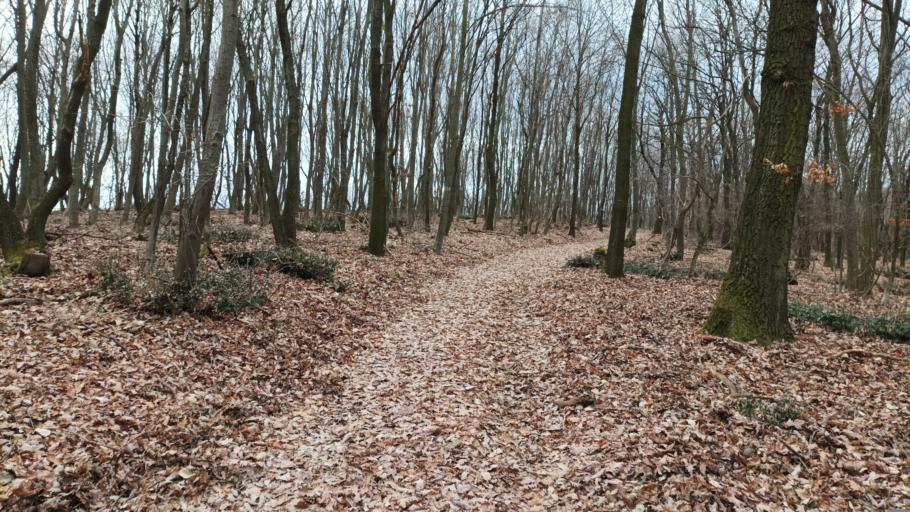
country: HU
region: Tolna
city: Szentgalpuszta
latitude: 46.3326
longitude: 18.6351
